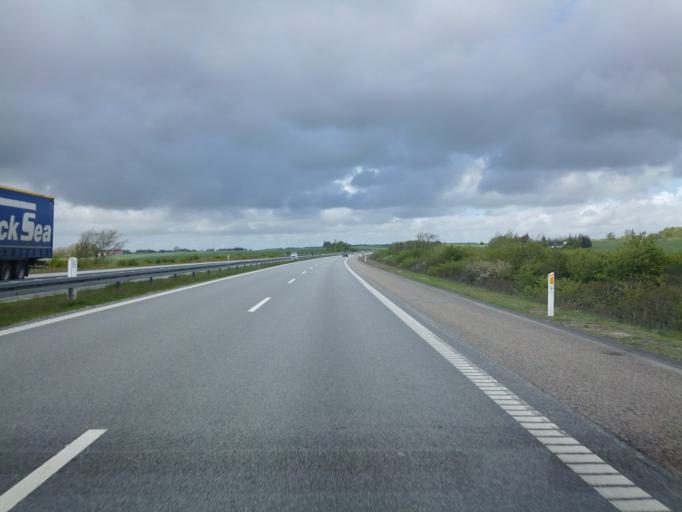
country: DK
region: North Denmark
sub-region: Bronderslev Kommune
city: Hjallerup
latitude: 57.1894
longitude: 10.1977
